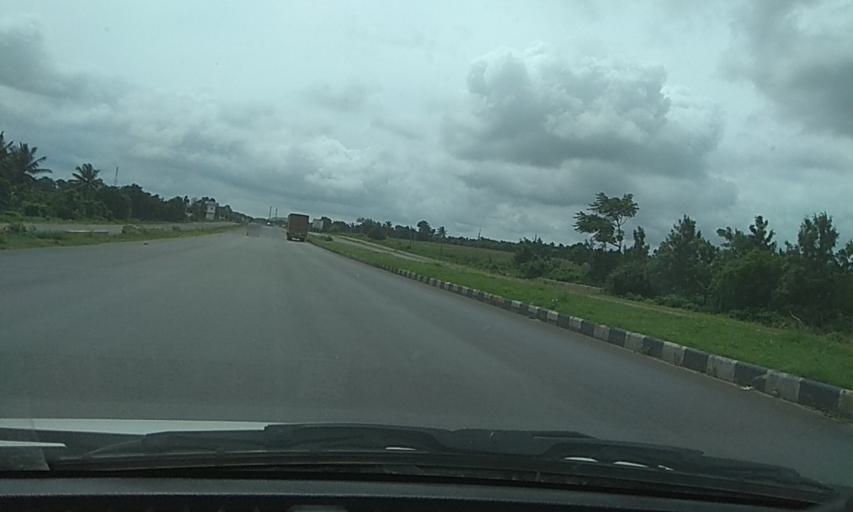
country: IN
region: Karnataka
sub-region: Davanagere
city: Mayakonda
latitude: 14.3818
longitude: 76.0867
